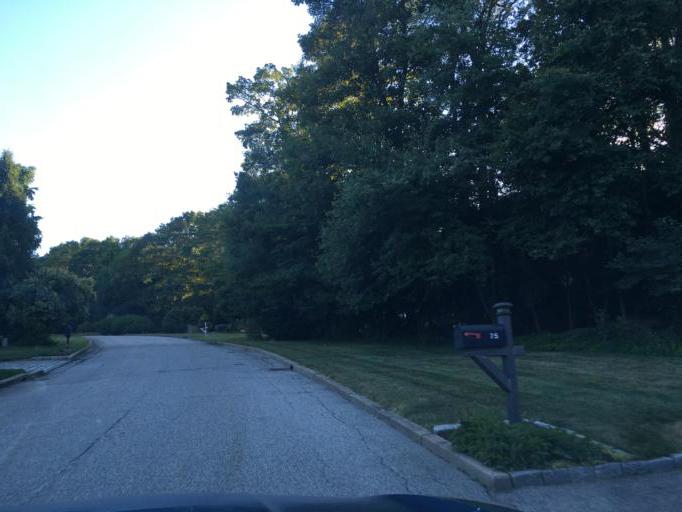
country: US
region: Rhode Island
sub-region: Washington County
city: Exeter
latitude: 41.6218
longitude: -71.5434
